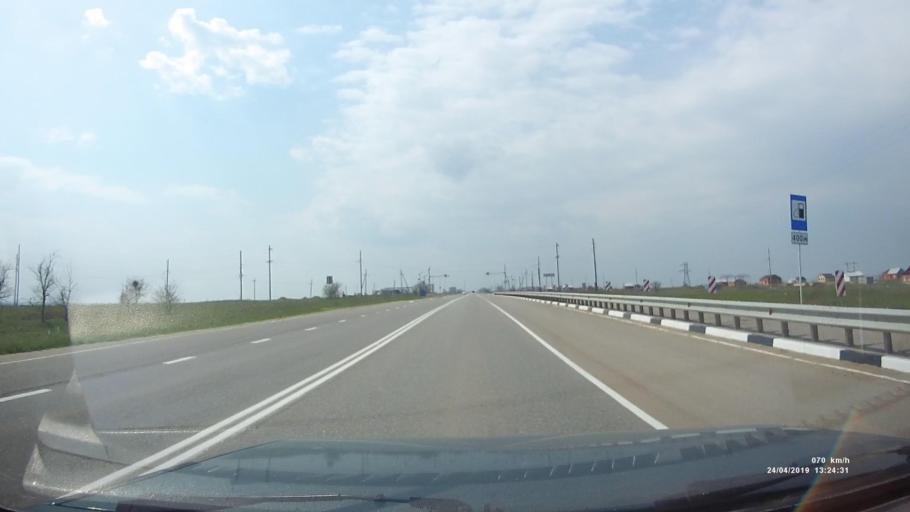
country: RU
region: Kalmykiya
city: Elista
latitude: 46.2845
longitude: 44.2539
